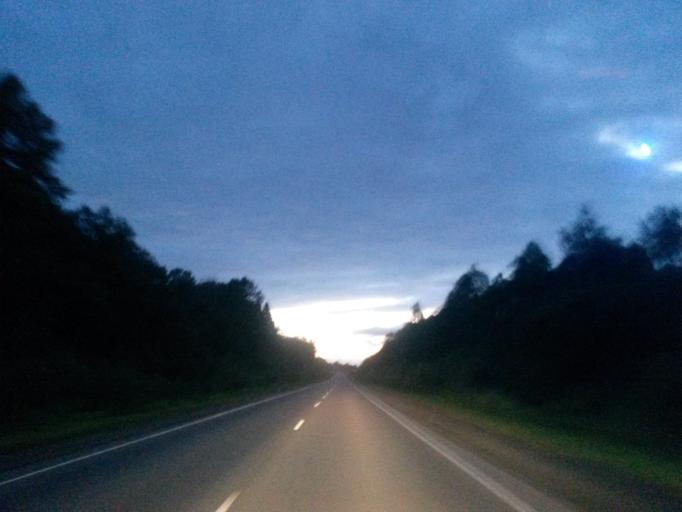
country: RU
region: Jaroslavl
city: Dubki
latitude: 57.2230
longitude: 40.2515
